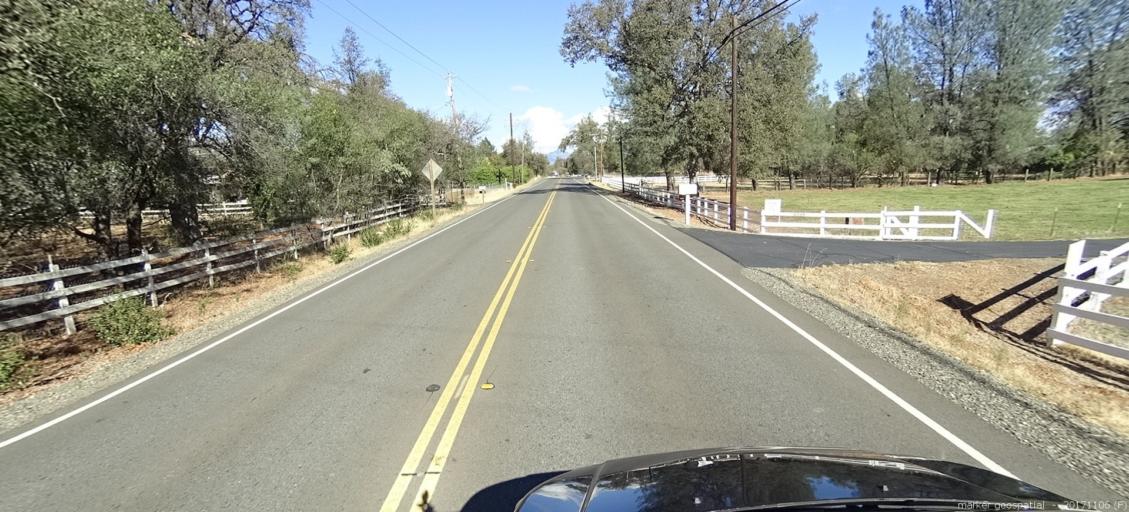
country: US
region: California
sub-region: Shasta County
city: Palo Cedro
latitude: 40.5894
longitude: -122.2390
